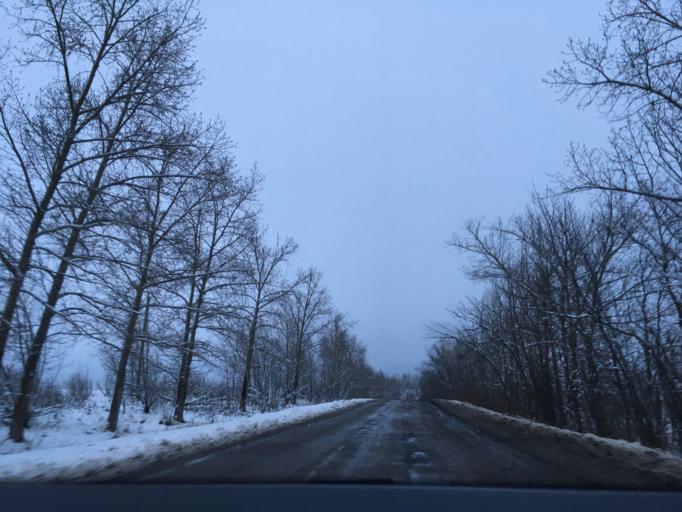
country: RU
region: Voronezj
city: Verkhniy Mamon
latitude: 50.0558
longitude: 40.2534
